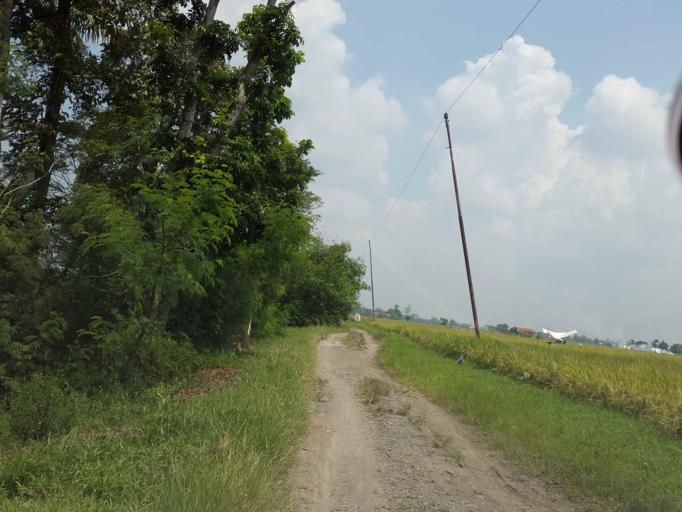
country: ID
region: Central Java
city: Dukuhkopi
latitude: -6.9619
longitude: 108.8284
